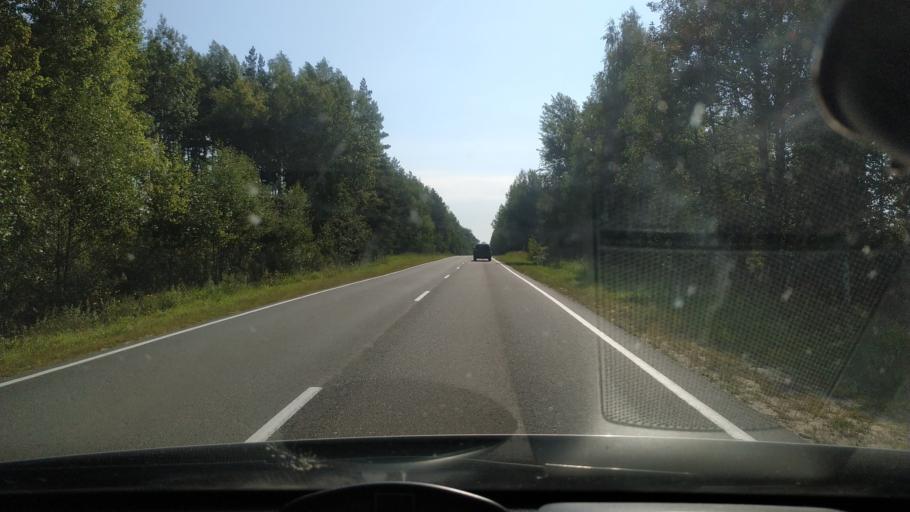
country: RU
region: Rjazan
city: Spas-Klepiki
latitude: 55.2219
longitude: 40.0814
